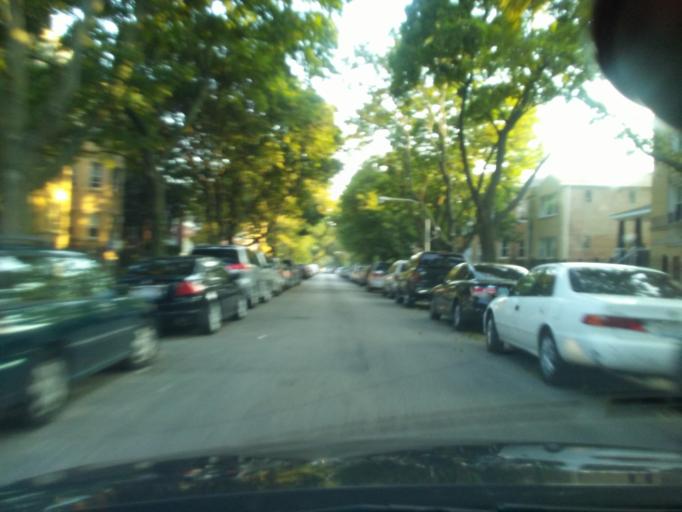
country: US
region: Illinois
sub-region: Cook County
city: Lincolnwood
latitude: 41.9945
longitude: -87.6983
